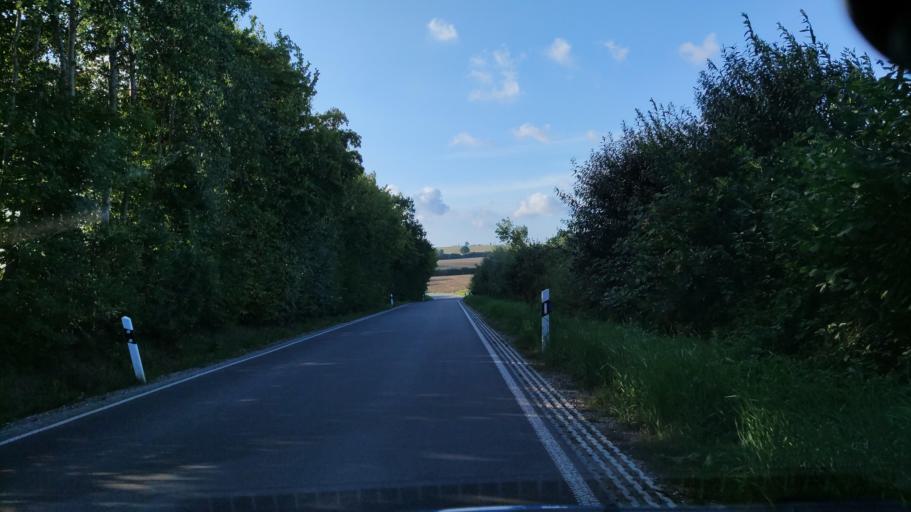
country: DE
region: Schleswig-Holstein
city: Glasau
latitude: 54.0930
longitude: 10.4911
